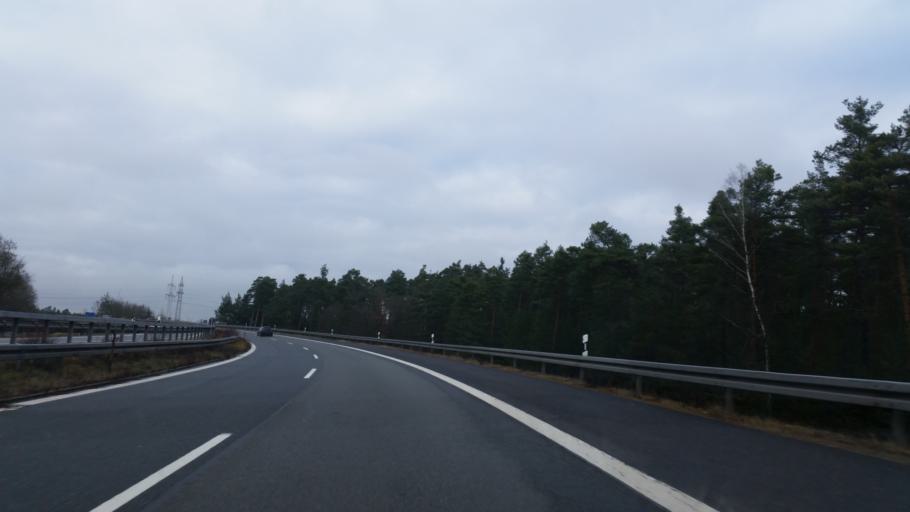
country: DE
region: Bavaria
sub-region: Regierungsbezirk Mittelfranken
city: Feucht
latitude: 49.3473
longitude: 11.2059
